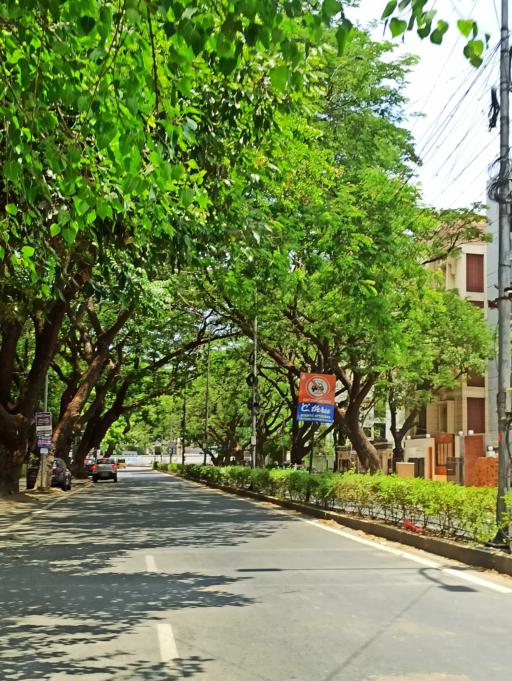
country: IN
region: Tamil Nadu
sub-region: Thiruvallur
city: Ambattur
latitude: 13.0829
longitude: 80.2003
